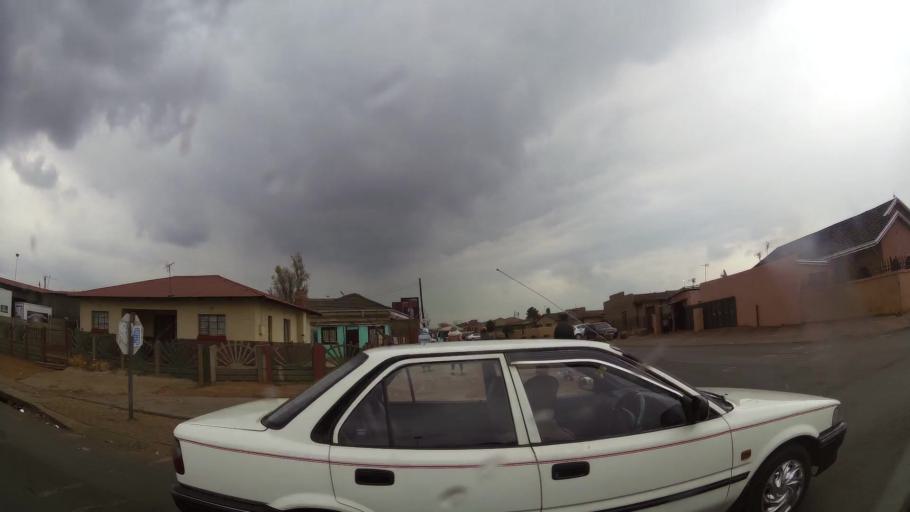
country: ZA
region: Gauteng
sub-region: Ekurhuleni Metropolitan Municipality
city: Germiston
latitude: -26.3261
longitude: 28.1532
